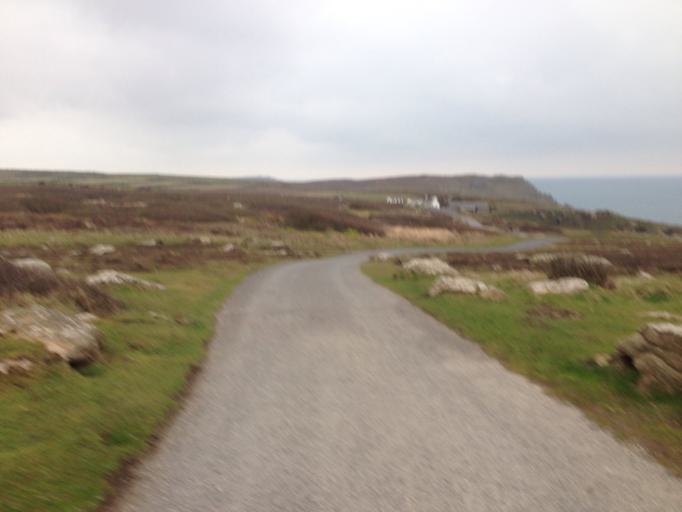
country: GB
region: England
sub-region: Cornwall
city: Sennen
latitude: 50.0652
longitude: -5.7123
